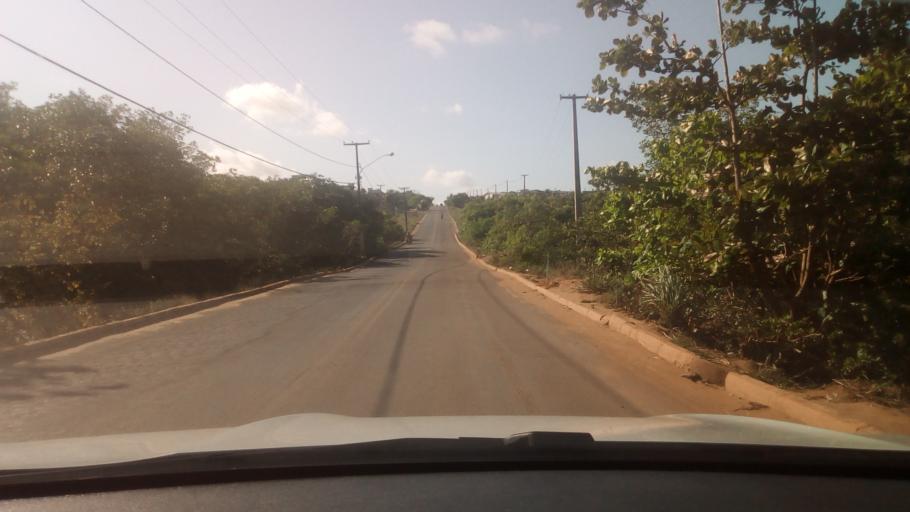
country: BR
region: Paraiba
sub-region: Conde
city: Conde
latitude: -7.2778
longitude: -34.8020
